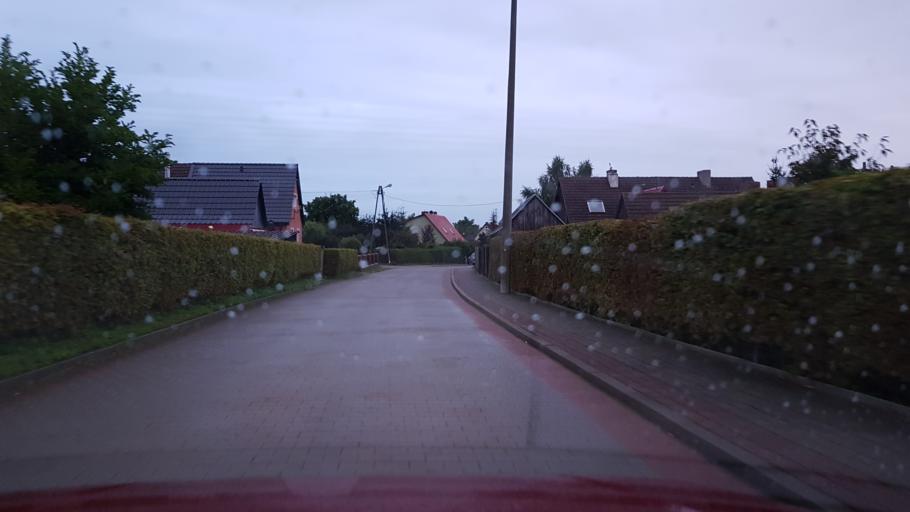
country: PL
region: West Pomeranian Voivodeship
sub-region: Powiat slawienski
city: Slawno
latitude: 54.3449
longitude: 16.6766
